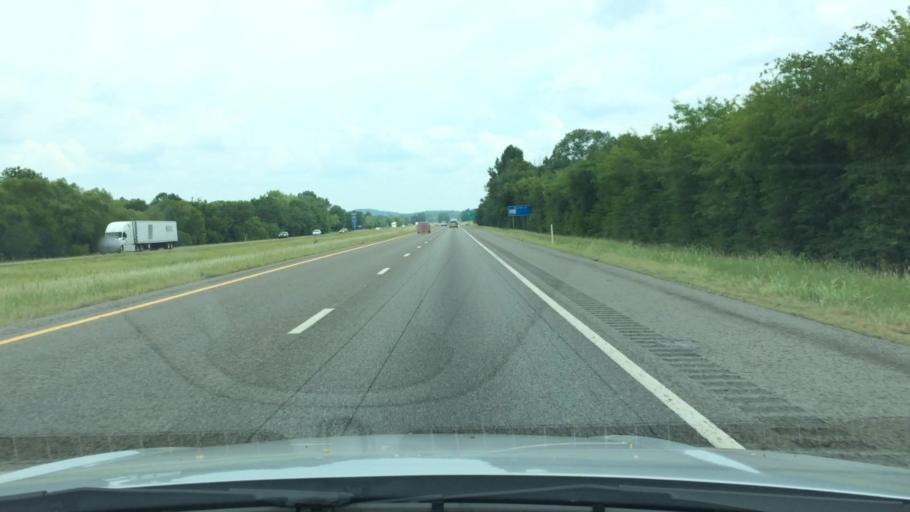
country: US
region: Tennessee
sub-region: Marshall County
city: Cornersville
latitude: 35.4295
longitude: -86.8794
